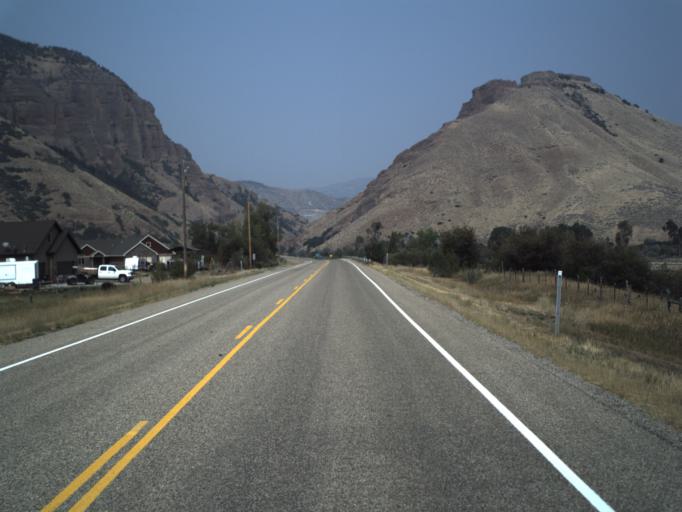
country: US
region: Utah
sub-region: Morgan County
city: Morgan
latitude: 41.0387
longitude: -111.5176
